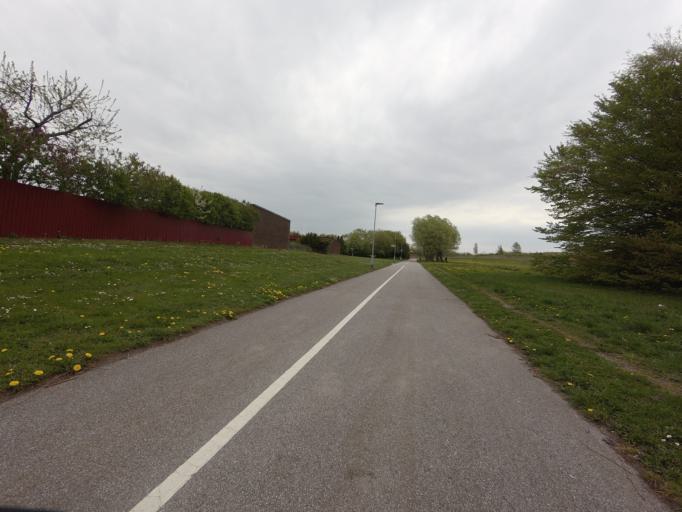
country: SE
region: Skane
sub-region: Malmo
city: Tygelsjo
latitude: 55.5527
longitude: 13.0273
